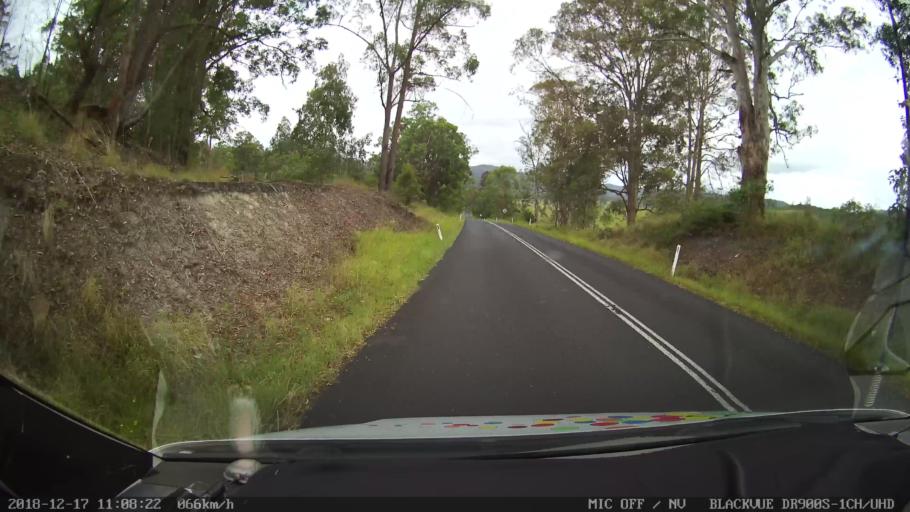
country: AU
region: New South Wales
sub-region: Kyogle
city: Kyogle
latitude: -28.7643
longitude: 152.6543
